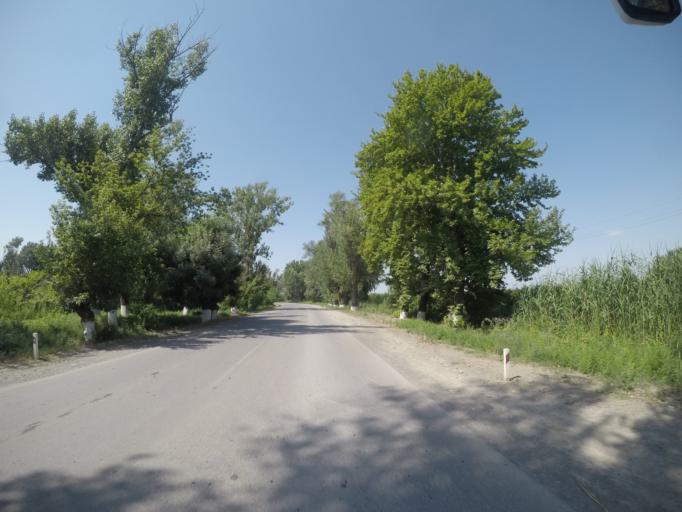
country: AZ
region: Agdas
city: Agdas
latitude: 40.6869
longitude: 47.5329
